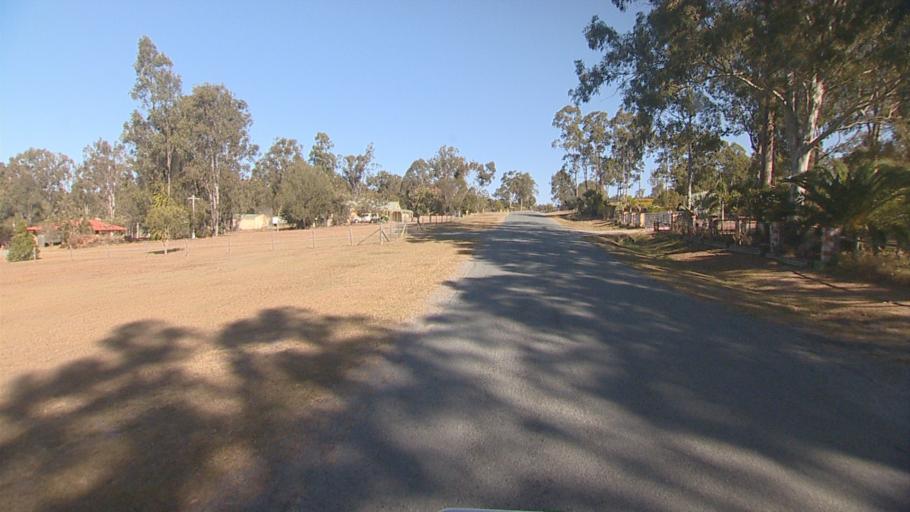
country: AU
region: Queensland
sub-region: Logan
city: Cedar Vale
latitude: -27.8618
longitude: 153.0354
